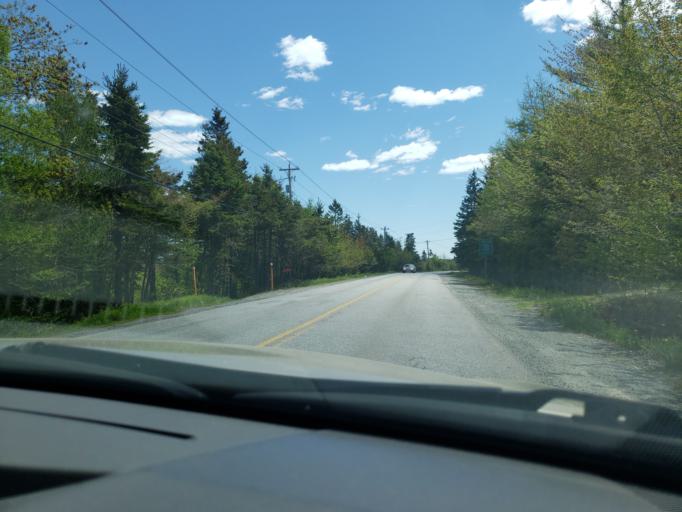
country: CA
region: Nova Scotia
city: Cole Harbour
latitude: 44.7313
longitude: -63.3076
